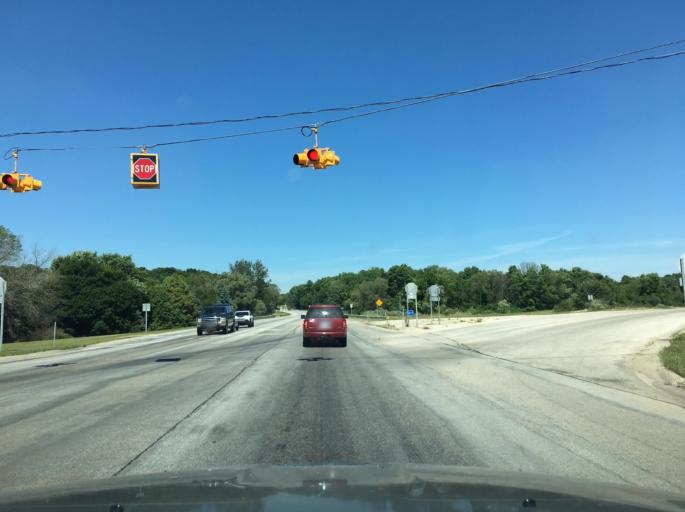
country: US
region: Michigan
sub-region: Osceola County
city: Reed City
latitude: 43.8840
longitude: -85.5109
